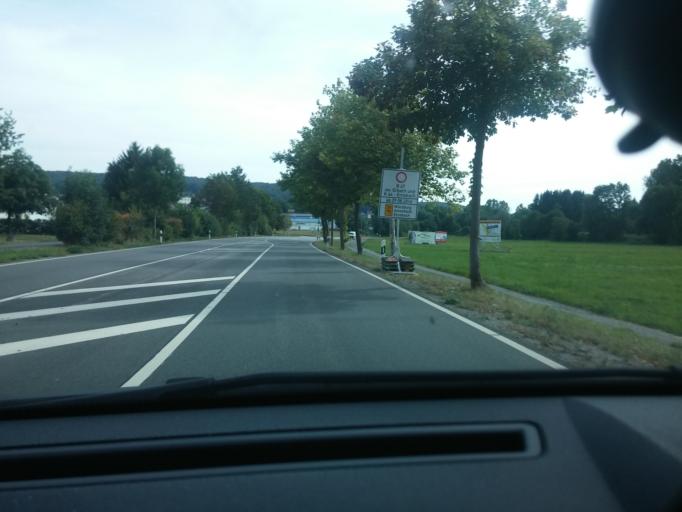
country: DE
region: Hesse
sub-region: Regierungsbezirk Darmstadt
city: Bad Konig
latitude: 49.7504
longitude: 9.0014
